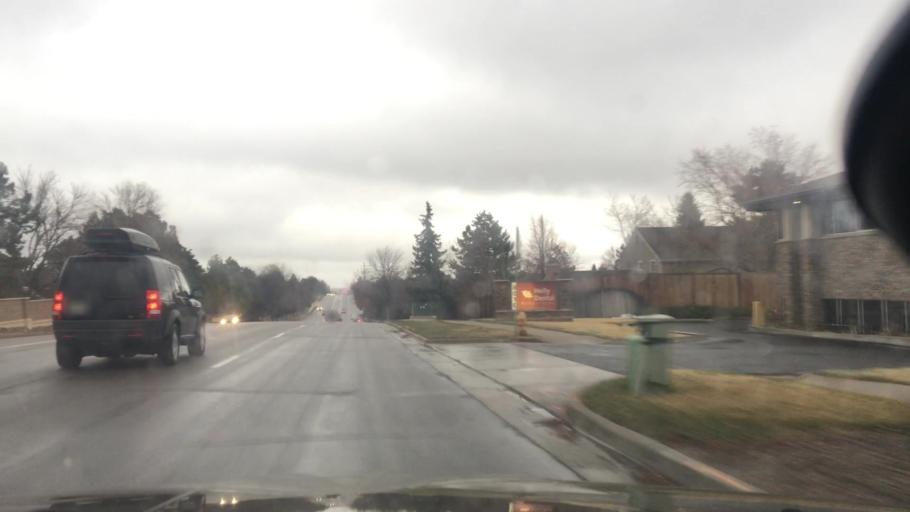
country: US
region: Colorado
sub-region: Arapahoe County
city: Castlewood
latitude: 39.5730
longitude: -104.9230
